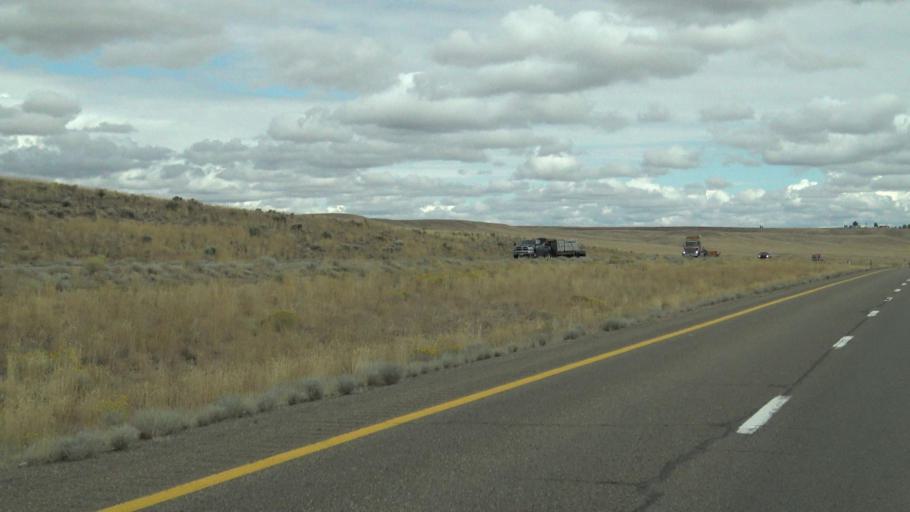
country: US
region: Nevada
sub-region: Elko County
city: Elko
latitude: 40.9100
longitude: -115.6959
